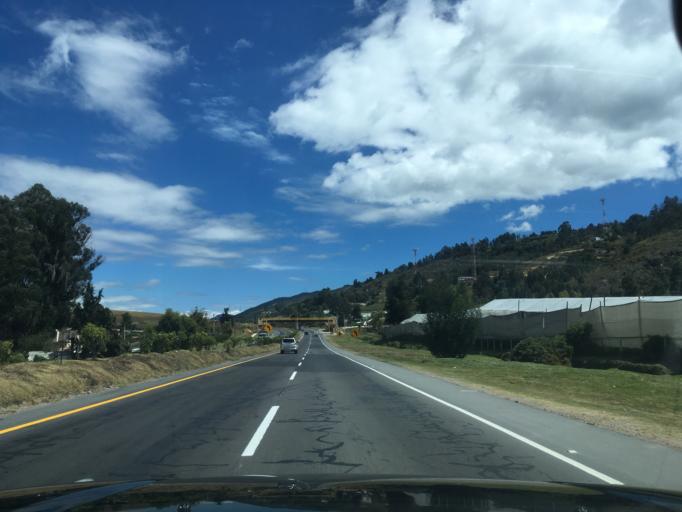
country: CO
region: Cundinamarca
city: Tocancipa
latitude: 4.9573
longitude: -73.9172
